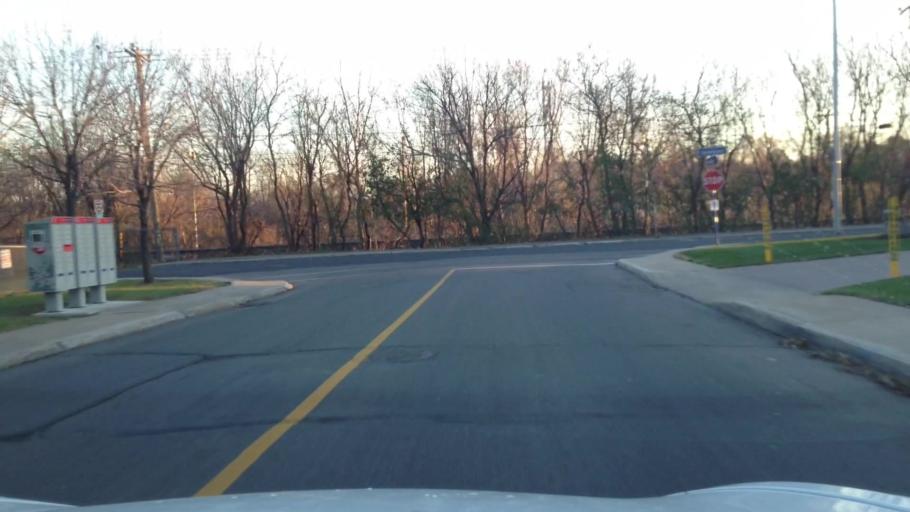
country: CA
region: Quebec
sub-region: Montreal
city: Pointe-Claire
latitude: 45.4395
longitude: -73.8330
